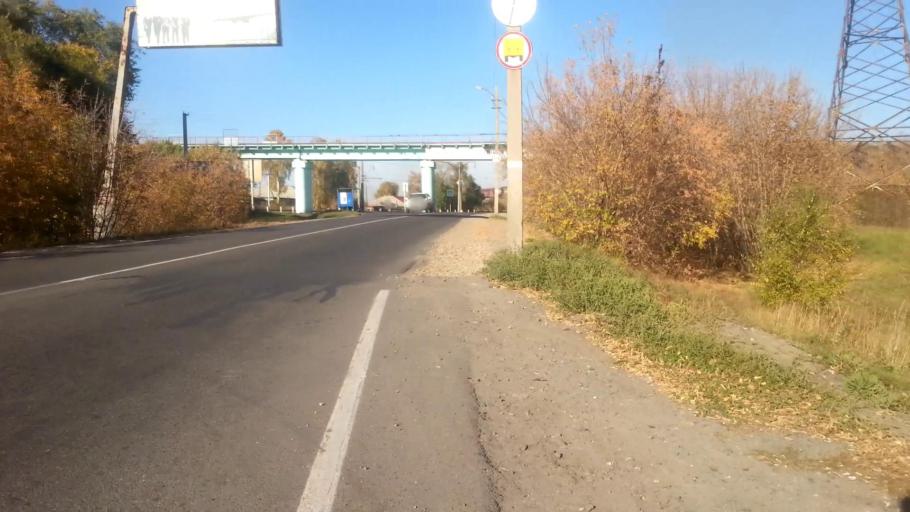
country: RU
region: Altai Krai
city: Novoaltaysk
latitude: 53.3747
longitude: 83.9348
